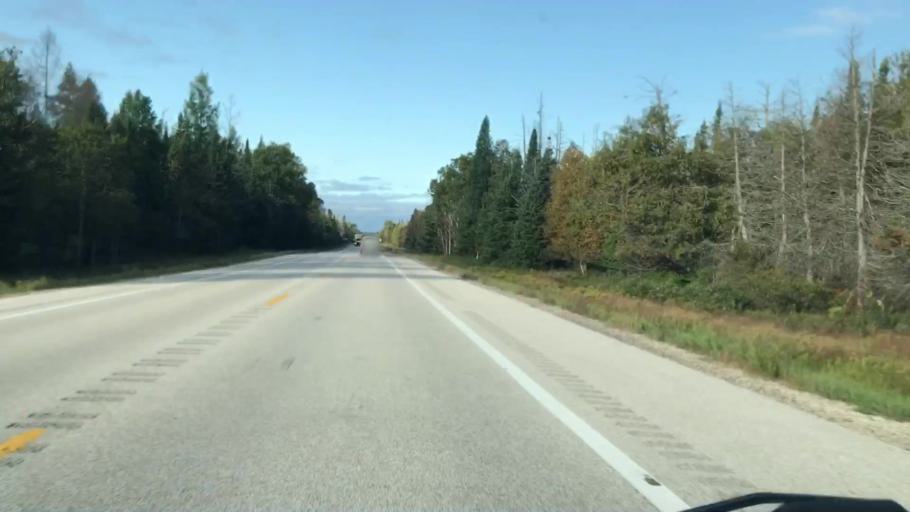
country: US
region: Michigan
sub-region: Luce County
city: Newberry
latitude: 46.3290
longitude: -85.1570
